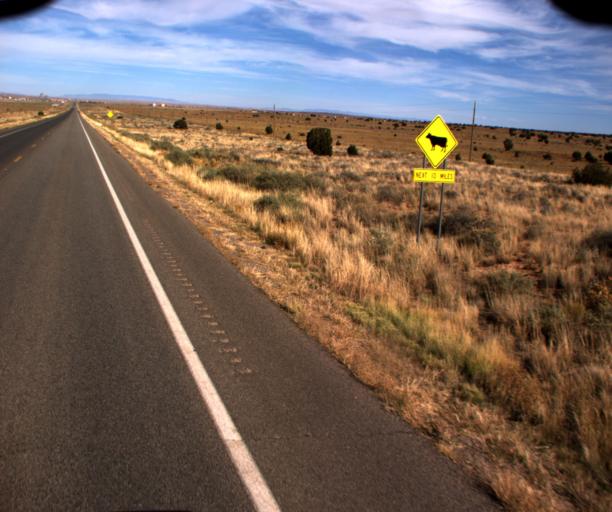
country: US
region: Arizona
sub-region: Navajo County
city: Kayenta
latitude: 36.7012
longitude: -110.2901
